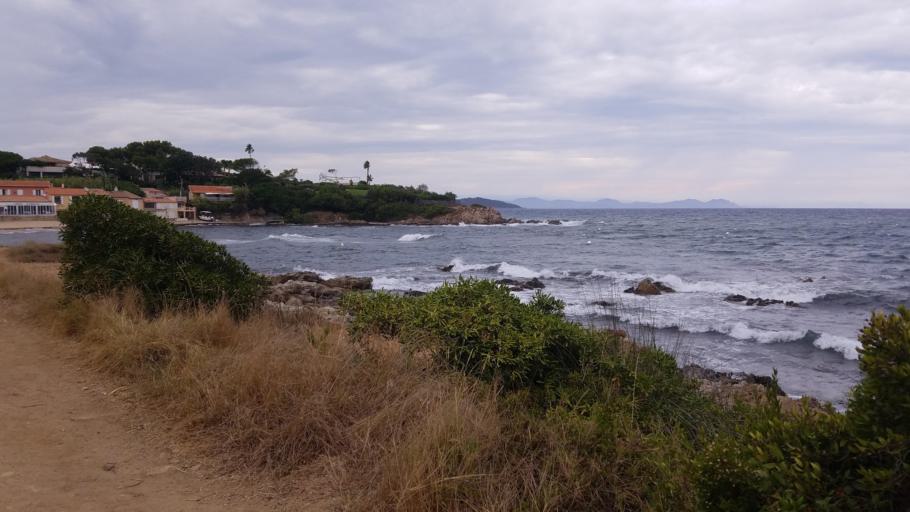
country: FR
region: Provence-Alpes-Cote d'Azur
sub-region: Departement du Var
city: Ramatuelle
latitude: 43.2072
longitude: 6.6683
